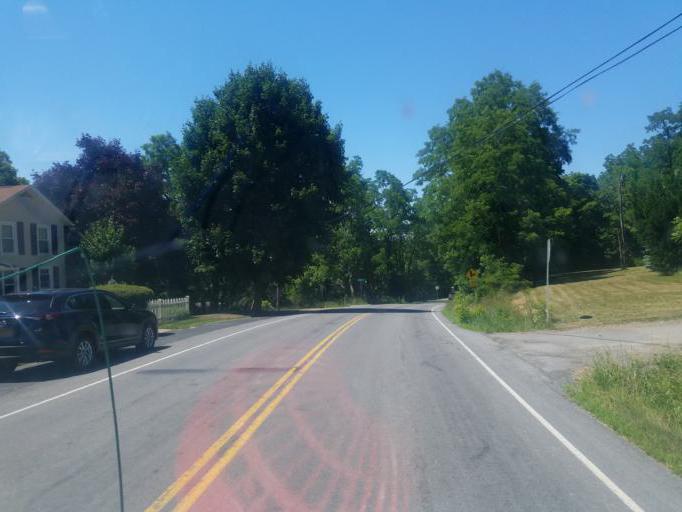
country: US
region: New York
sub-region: Yates County
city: Penn Yan
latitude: 42.7549
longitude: -77.0128
